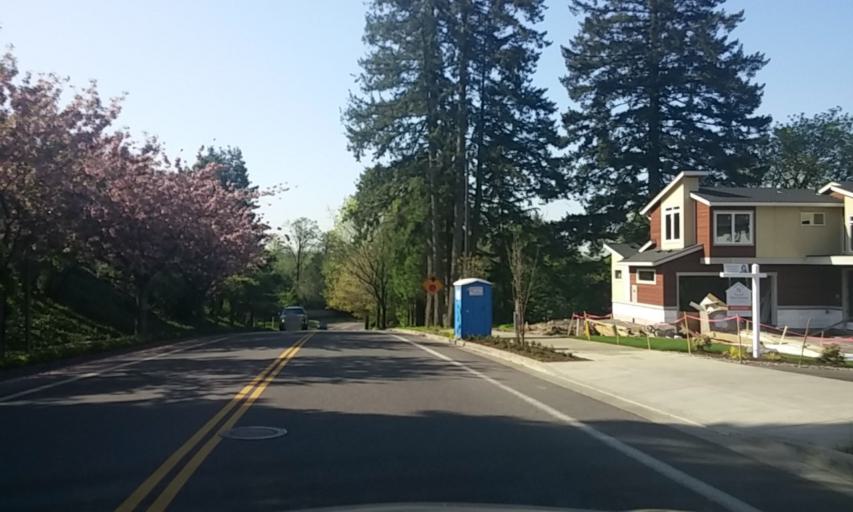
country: US
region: Oregon
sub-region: Washington County
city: Durham
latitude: 45.4274
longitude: -122.7334
